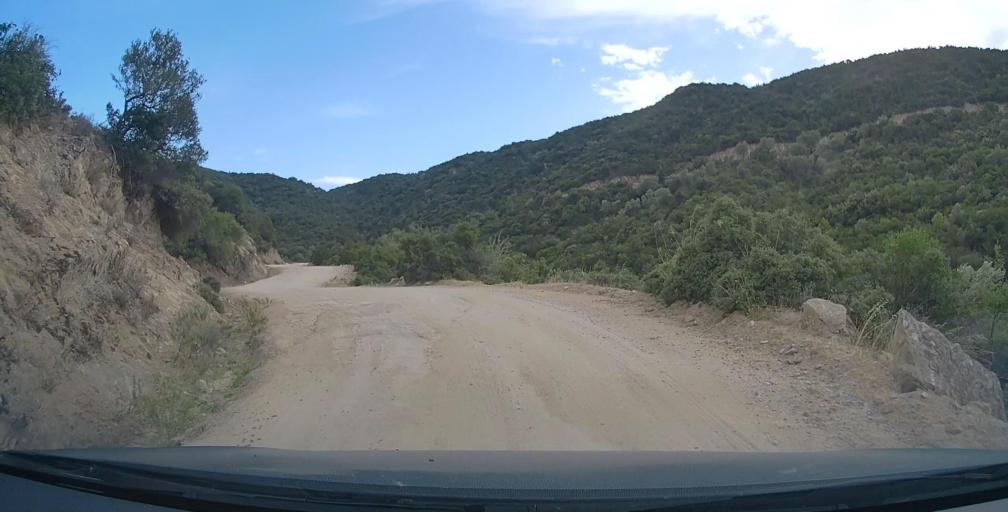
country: GR
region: Central Macedonia
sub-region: Nomos Chalkidikis
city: Sykia
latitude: 40.0147
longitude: 23.9389
